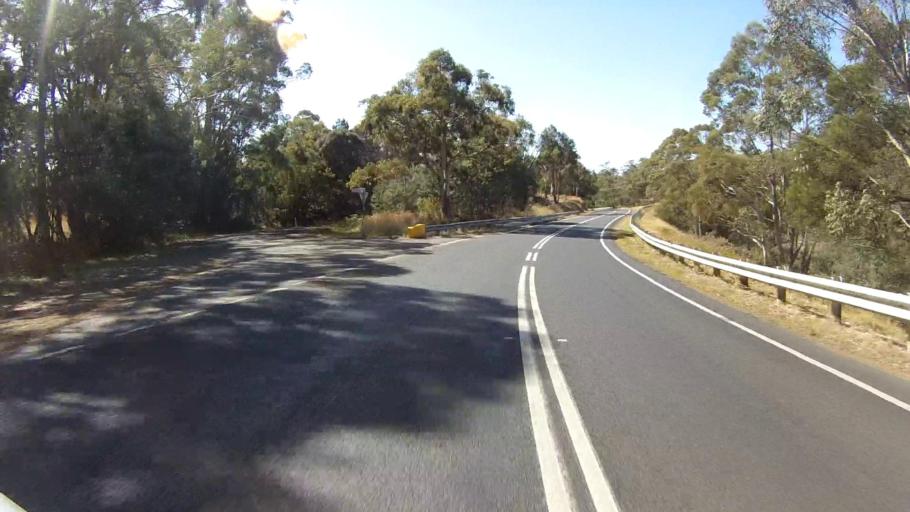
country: AU
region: Tasmania
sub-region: Sorell
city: Sorell
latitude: -42.3937
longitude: 147.9330
